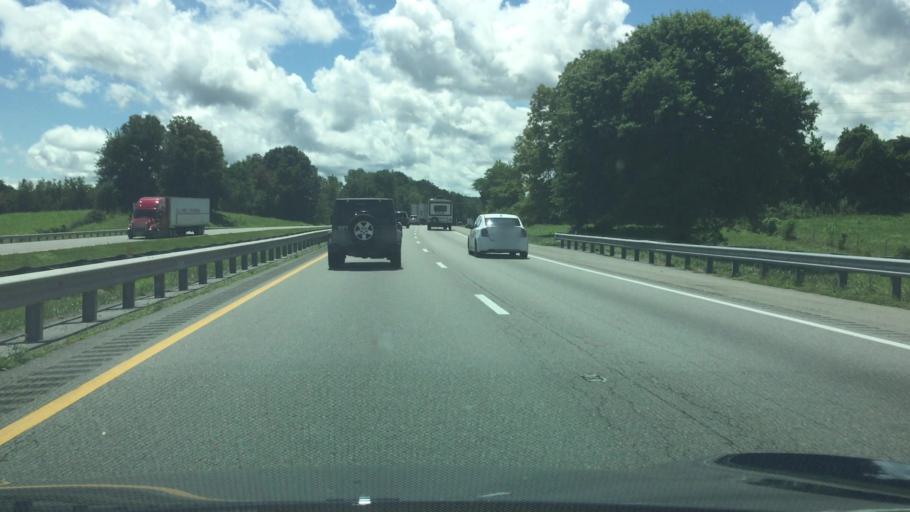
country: US
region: Virginia
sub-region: Washington County
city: Abingdon
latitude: 36.7201
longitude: -81.9192
